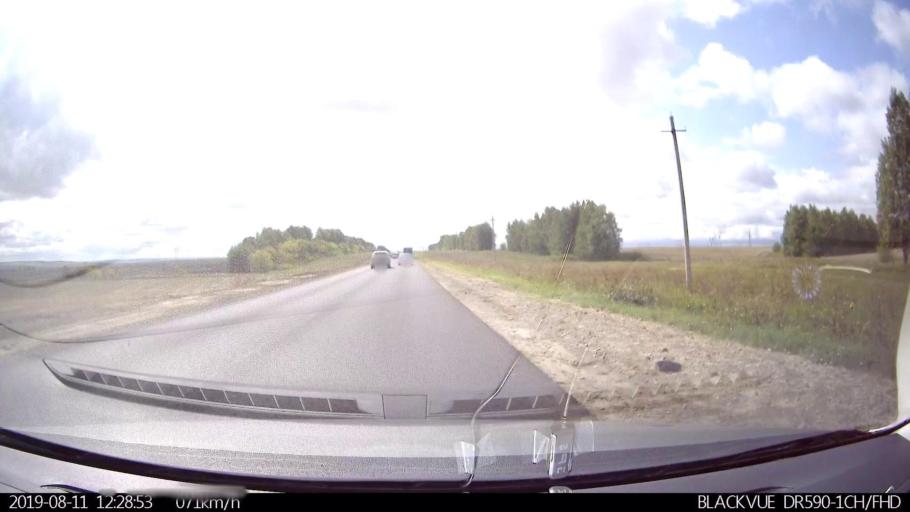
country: RU
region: Ulyanovsk
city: Ignatovka
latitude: 53.8398
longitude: 47.9082
